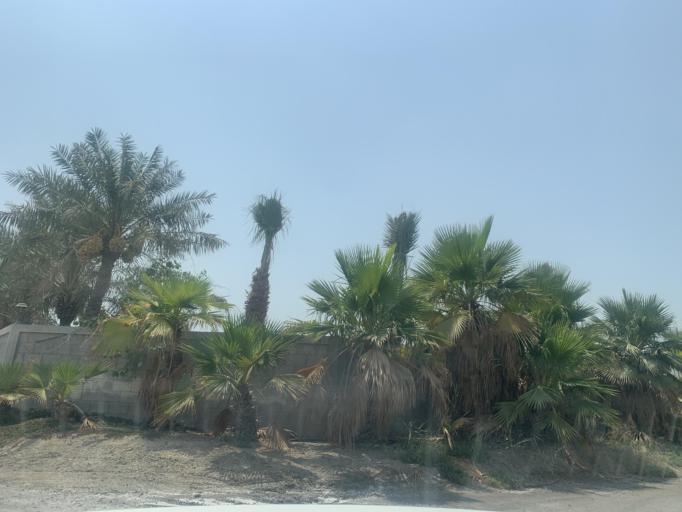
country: BH
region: Central Governorate
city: Madinat Hamad
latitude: 26.1229
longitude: 50.4666
